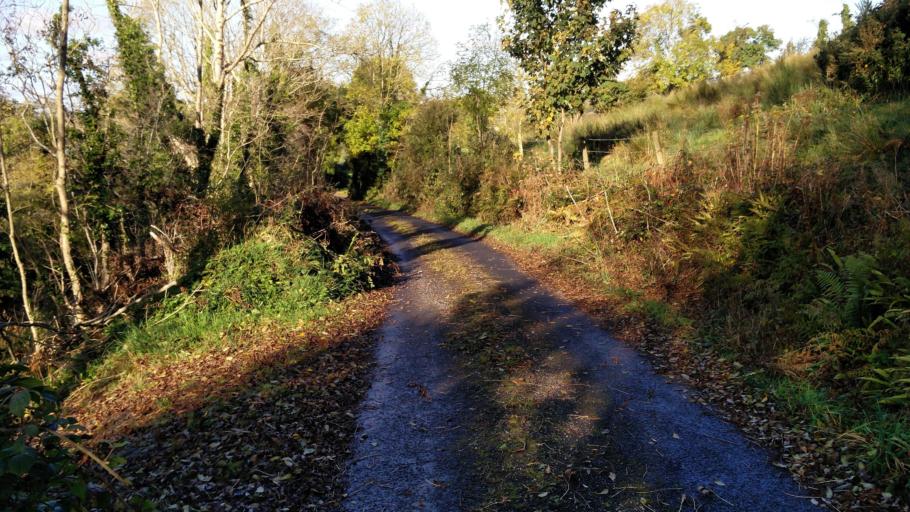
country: IE
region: Connaught
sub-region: Maigh Eo
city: Westport
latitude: 53.7828
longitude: -9.4576
